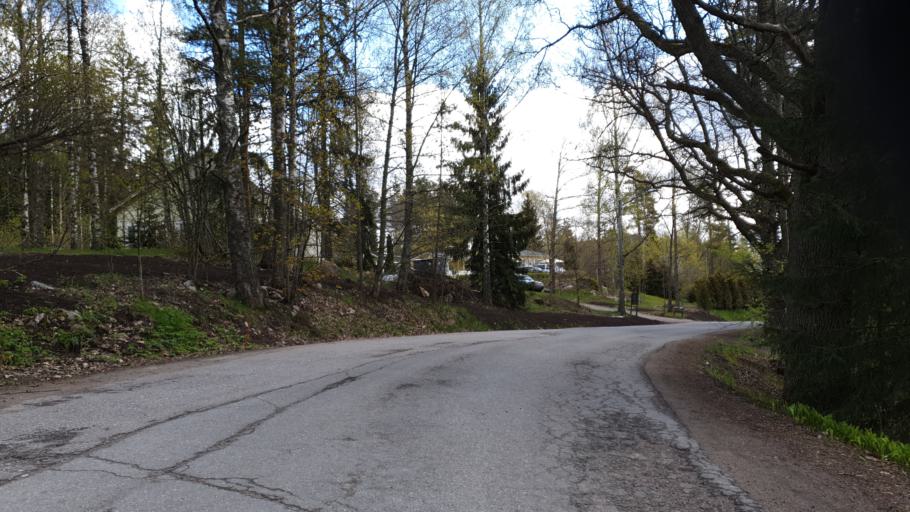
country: FI
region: Uusimaa
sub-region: Helsinki
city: Nurmijaervi
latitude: 60.3487
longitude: 24.8553
